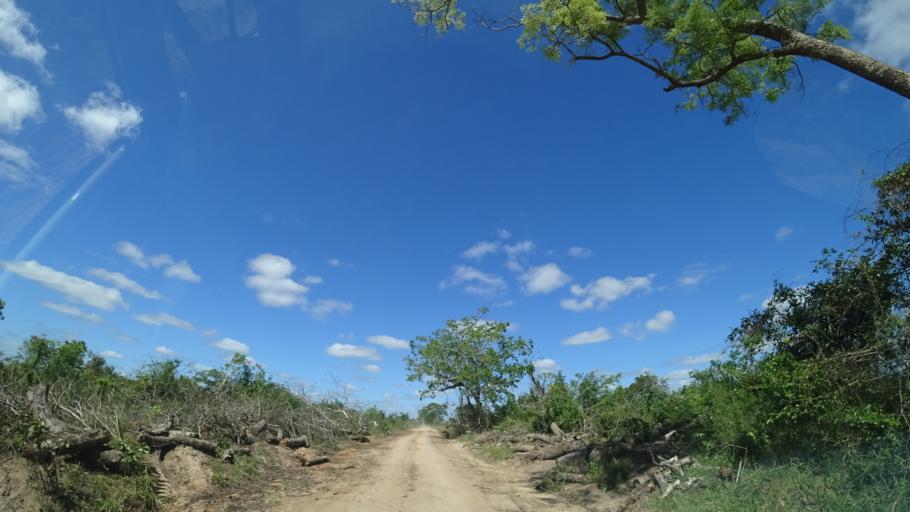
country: MZ
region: Sofala
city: Dondo
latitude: -19.2837
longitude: 34.6854
